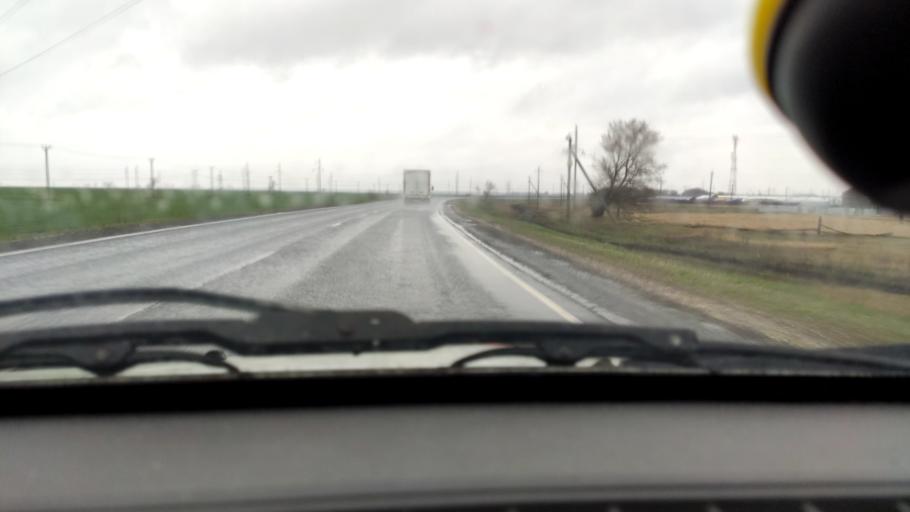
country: RU
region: Samara
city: Povolzhskiy
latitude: 53.6344
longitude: 49.6585
